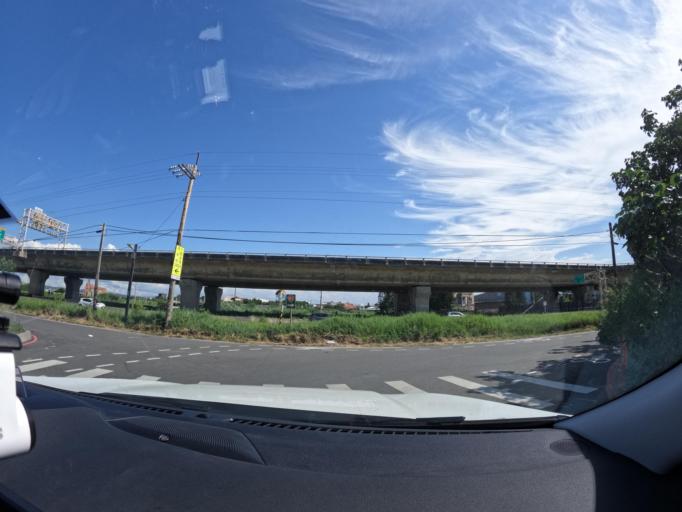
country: TW
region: Taiwan
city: Taoyuan City
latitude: 25.1123
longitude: 121.2395
